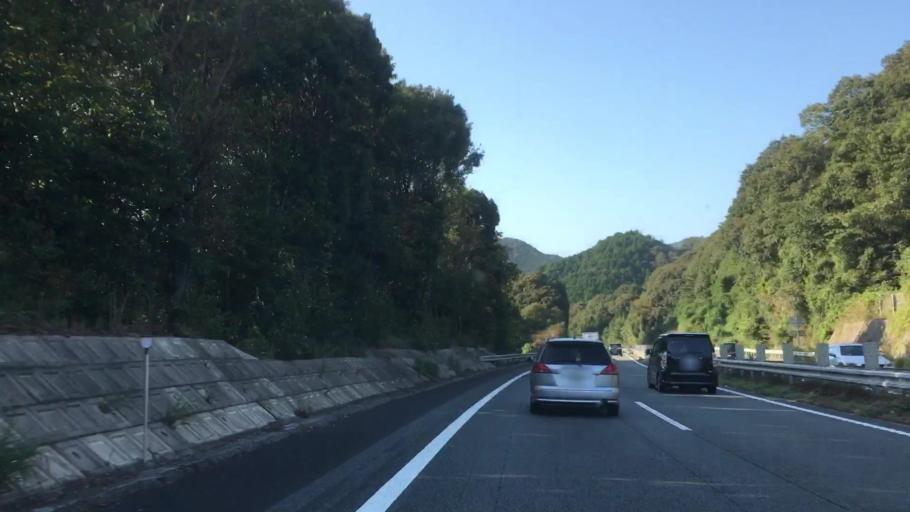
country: JP
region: Yamaguchi
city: Ogori-shimogo
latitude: 34.1313
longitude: 131.3768
